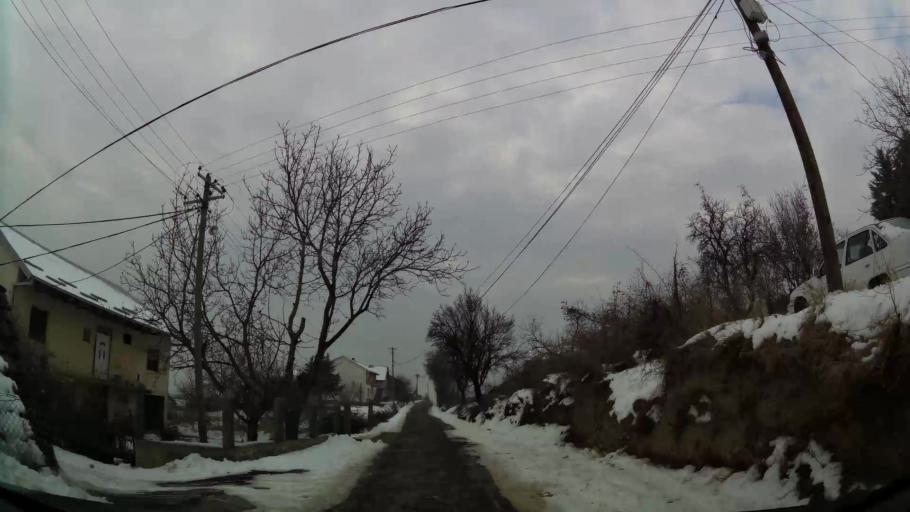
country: MK
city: Kondovo
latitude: 42.0407
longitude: 21.3437
